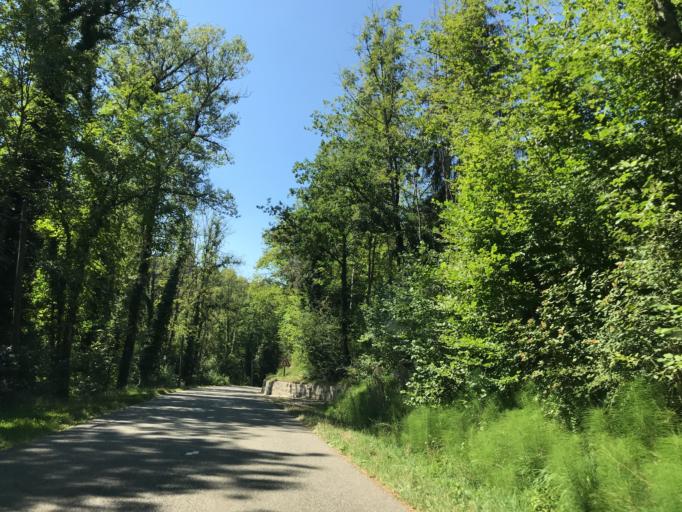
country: FR
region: Rhone-Alpes
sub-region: Departement de la Haute-Savoie
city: Villaz
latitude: 45.9275
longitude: 6.1820
